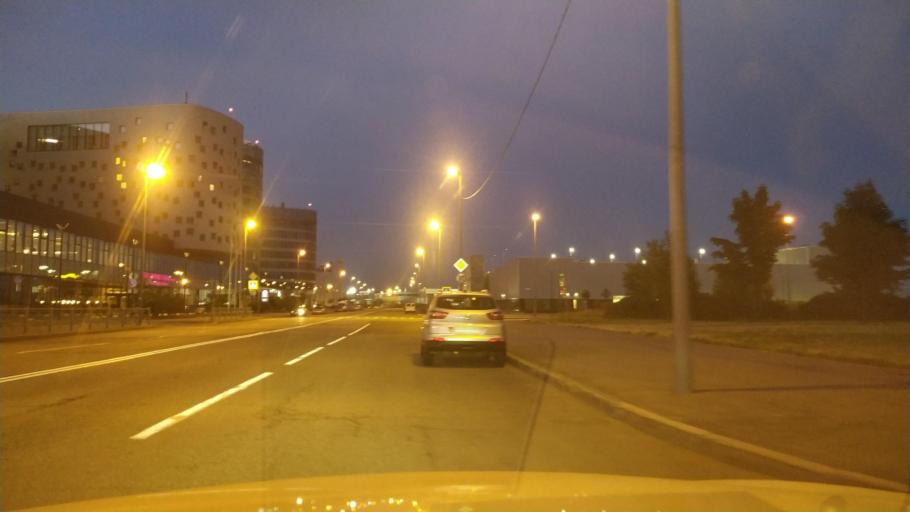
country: RU
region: St.-Petersburg
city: Kupchino
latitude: 59.8061
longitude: 30.3140
